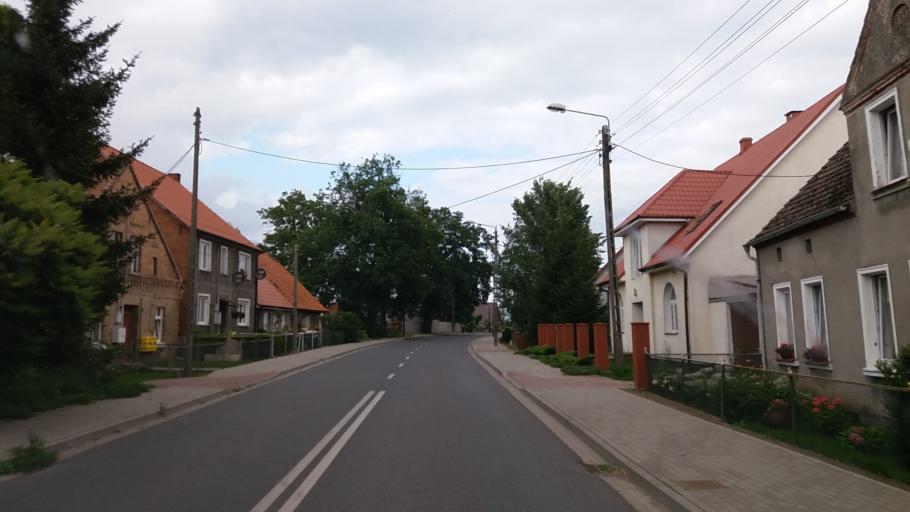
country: PL
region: West Pomeranian Voivodeship
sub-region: Powiat choszczenski
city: Choszczno
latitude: 53.1288
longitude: 15.3749
